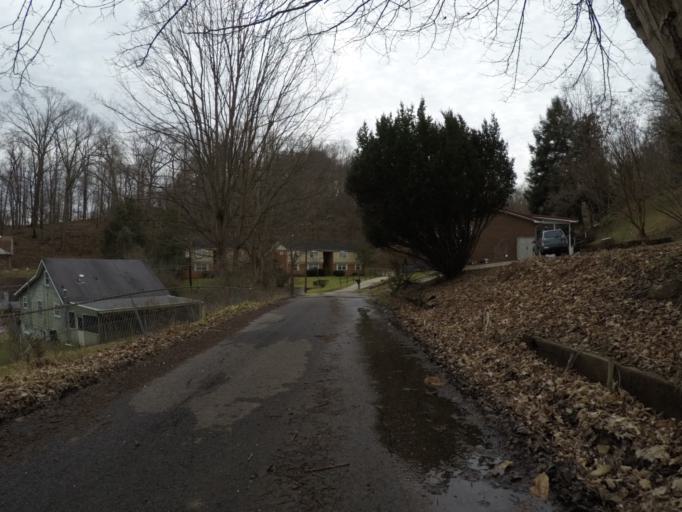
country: US
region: Ohio
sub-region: Lawrence County
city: Burlington
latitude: 38.3895
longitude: -82.5152
